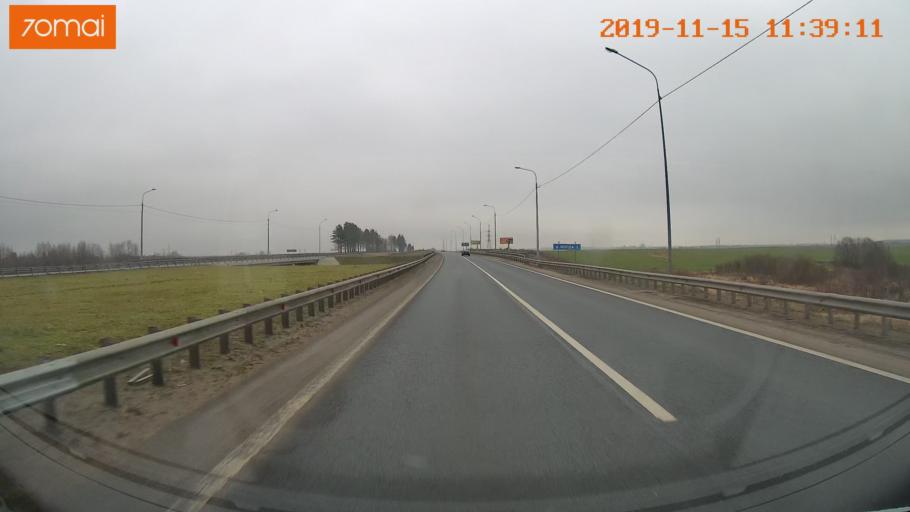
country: RU
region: Vologda
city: Molochnoye
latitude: 59.2110
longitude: 39.7174
